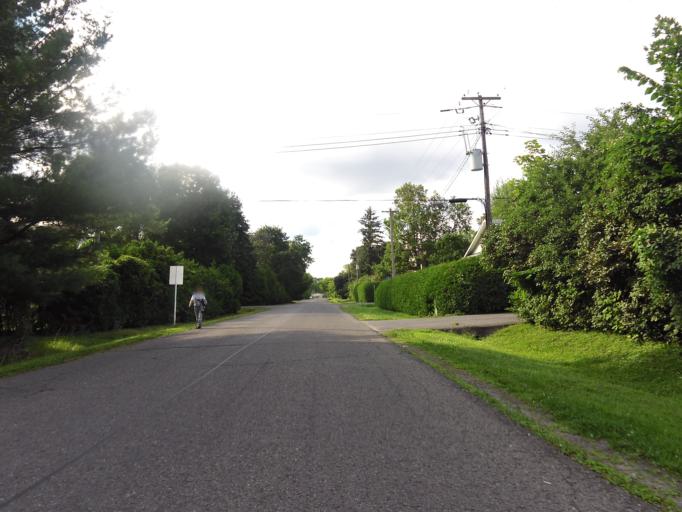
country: CA
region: Ontario
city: Ottawa
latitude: 45.3561
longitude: -75.7426
